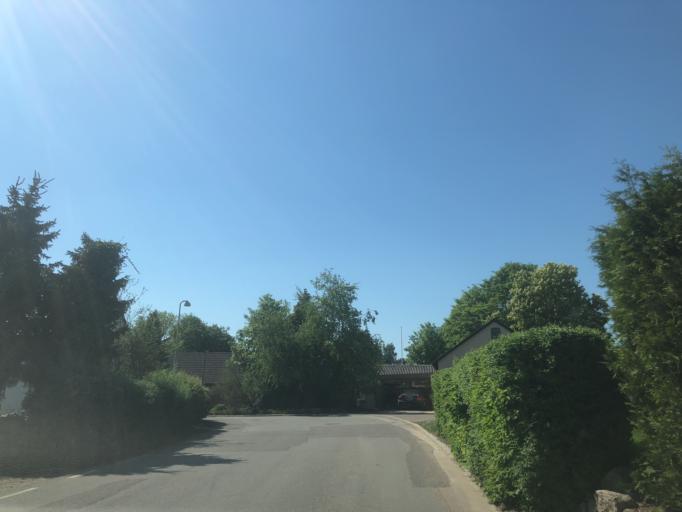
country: DK
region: Zealand
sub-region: Greve Kommune
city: Tune
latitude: 55.6251
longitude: 12.1915
